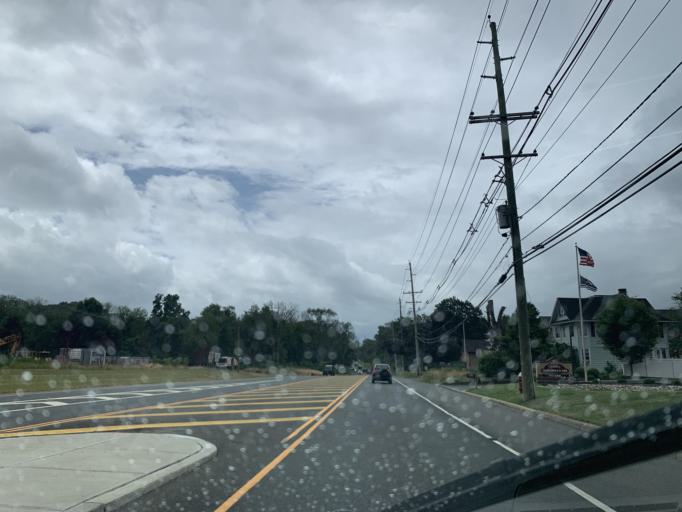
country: US
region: New Jersey
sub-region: Somerset County
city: Bloomingdale
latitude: 40.4763
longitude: -74.6561
